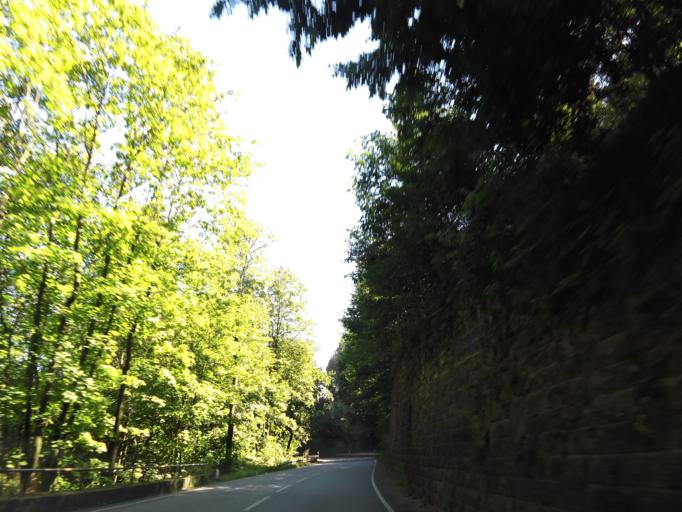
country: DE
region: Saxony
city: Kurort Gohrisch
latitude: 50.9257
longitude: 14.1147
